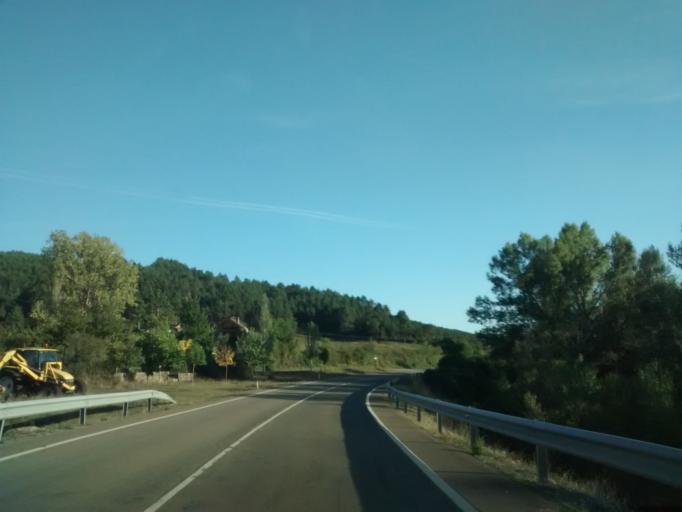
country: ES
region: Aragon
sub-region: Provincia de Huesca
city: Anso
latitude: 42.7260
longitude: -0.7526
